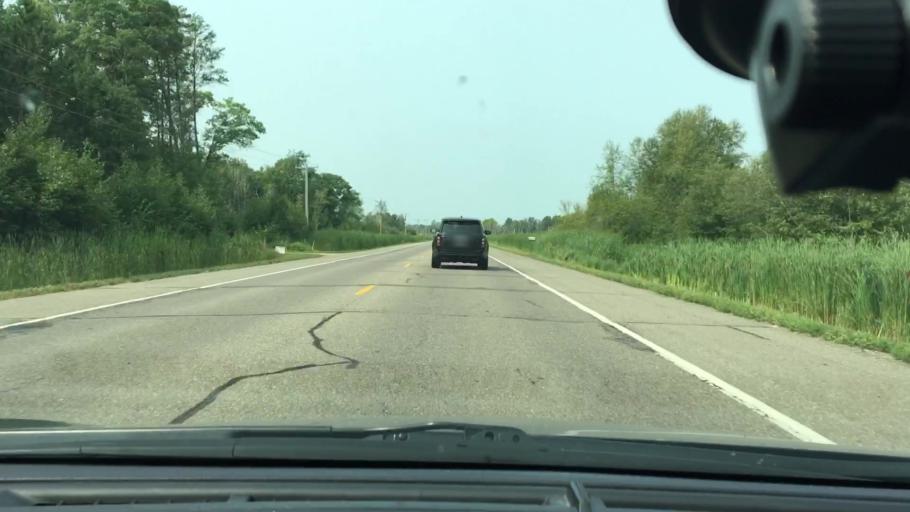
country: US
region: Minnesota
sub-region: Crow Wing County
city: Brainerd
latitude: 46.3985
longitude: -94.2146
